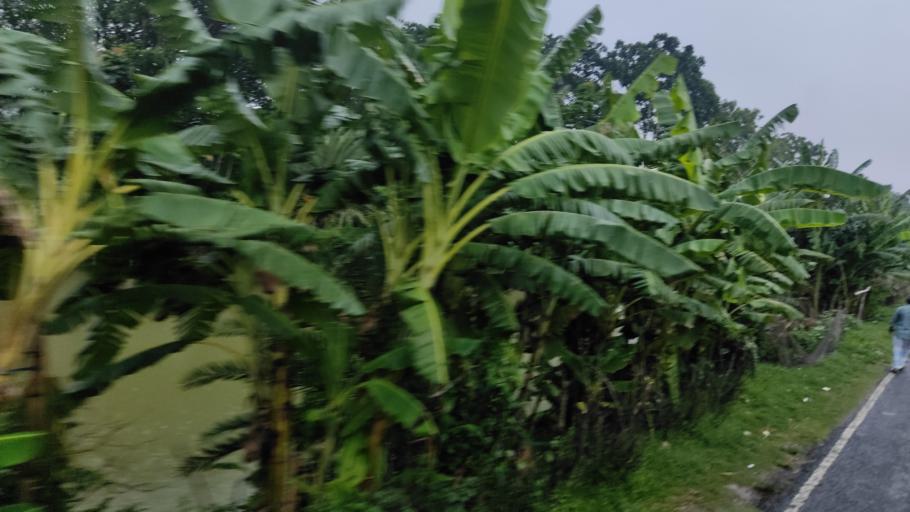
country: BD
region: Barisal
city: Bhandaria
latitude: 22.3118
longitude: 90.3251
